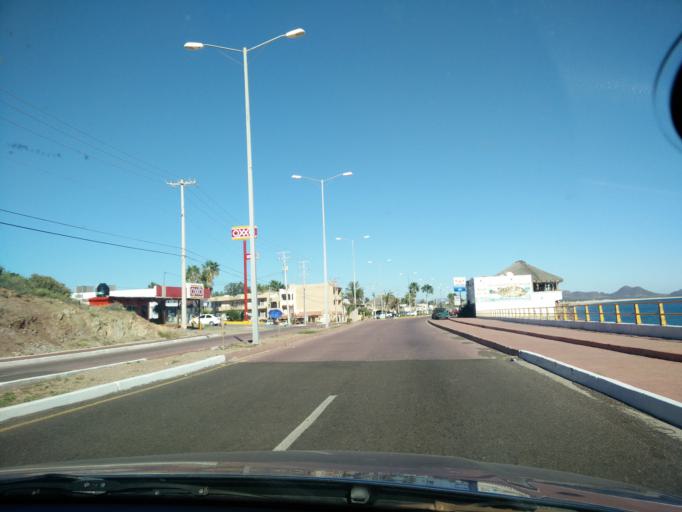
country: MX
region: Sonora
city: Heroica Guaymas
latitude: 27.9623
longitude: -111.0269
